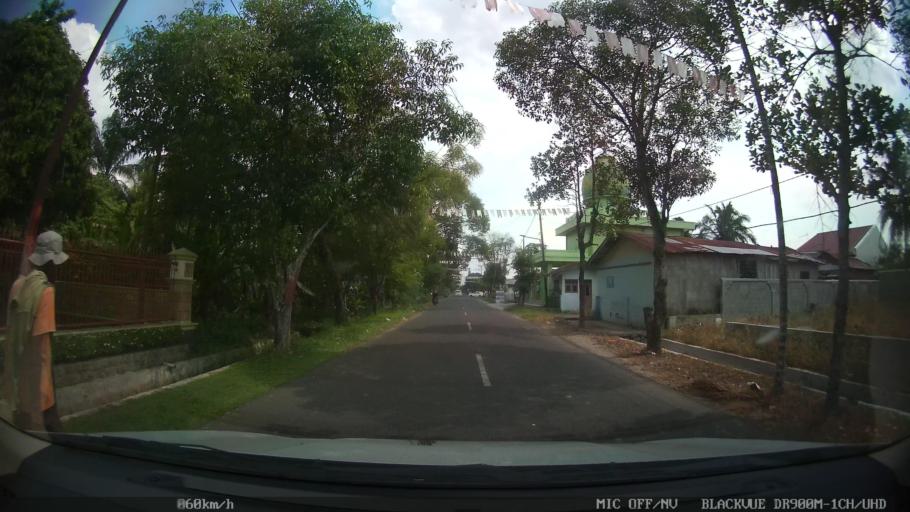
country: ID
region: North Sumatra
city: Binjai
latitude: 3.6330
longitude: 98.5026
